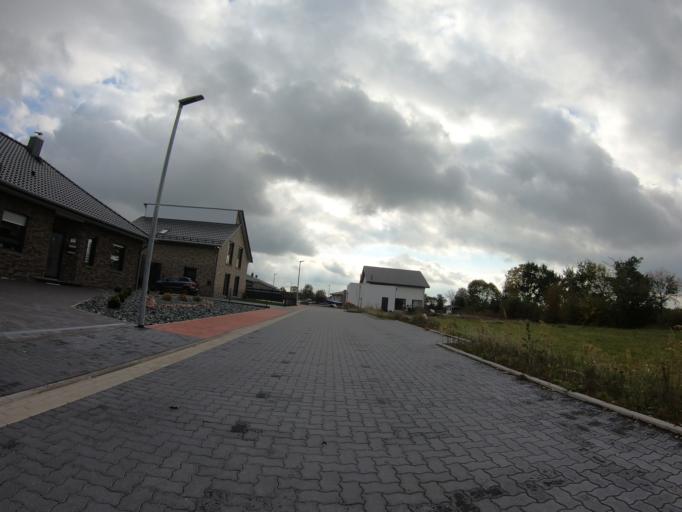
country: DE
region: Lower Saxony
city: Wahrenholz
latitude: 52.6185
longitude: 10.5916
